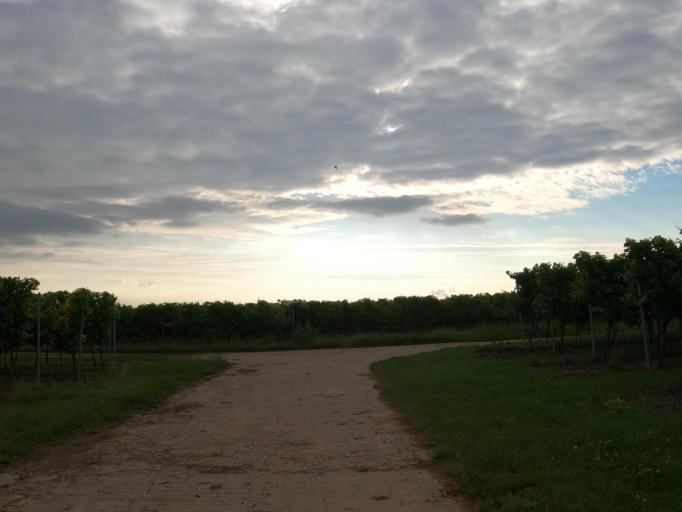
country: DE
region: Rheinland-Pfalz
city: Kirchheim an der Weinstrasse
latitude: 49.5311
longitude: 8.1850
